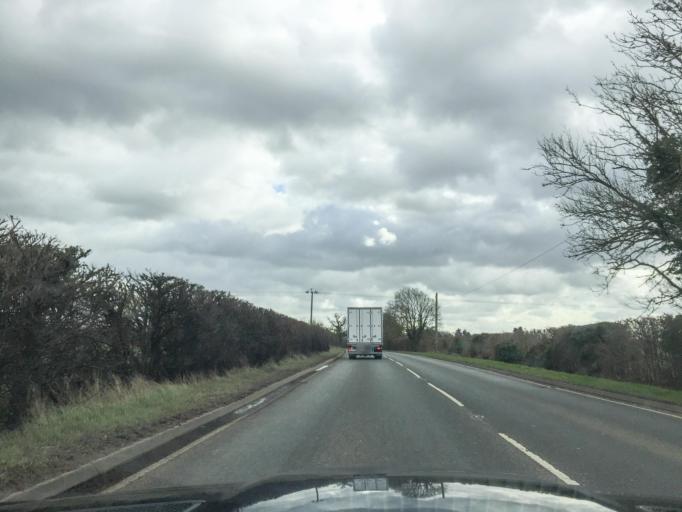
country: GB
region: England
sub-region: Warwickshire
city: Wellesbourne Mountford
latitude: 52.2181
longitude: -1.6019
